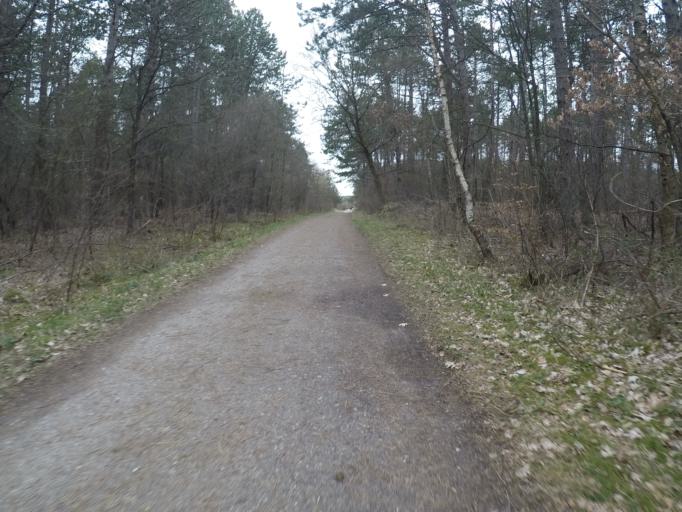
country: DE
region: Lower Saxony
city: Nordholz
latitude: 53.8219
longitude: 8.6442
